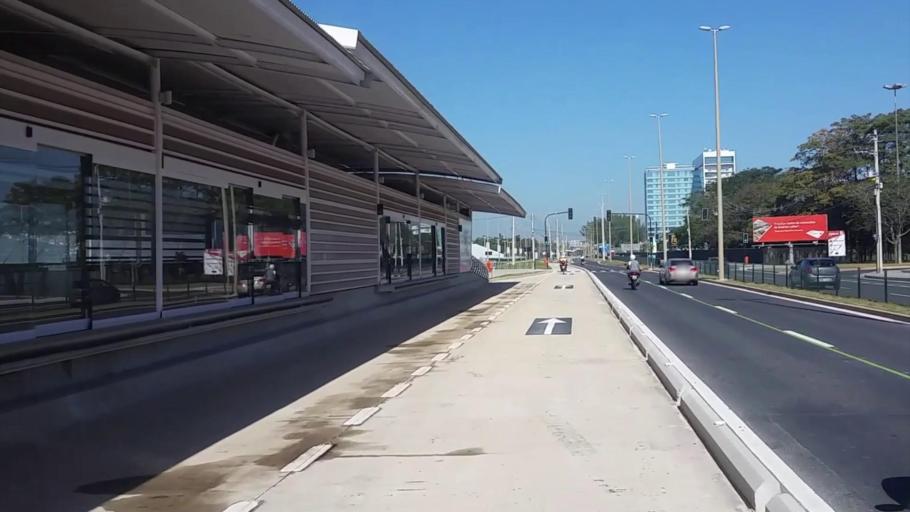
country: BR
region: Rio de Janeiro
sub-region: Nilopolis
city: Nilopolis
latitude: -22.9767
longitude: -43.4064
